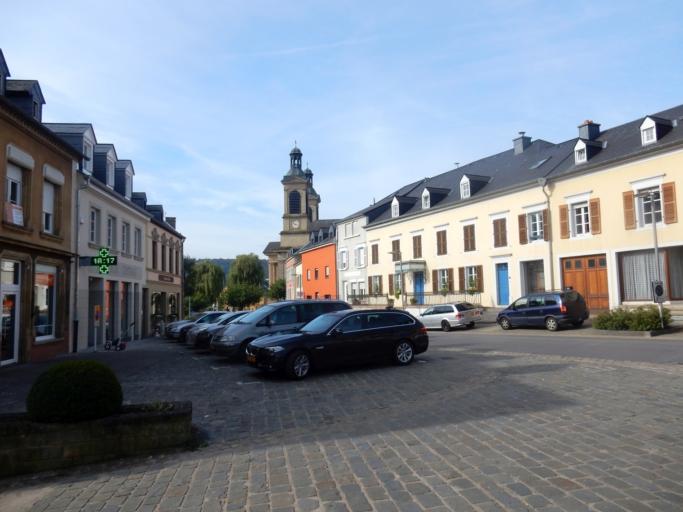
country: LU
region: Luxembourg
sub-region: Canton de Mersch
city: Mersch
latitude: 49.7472
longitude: 6.1039
